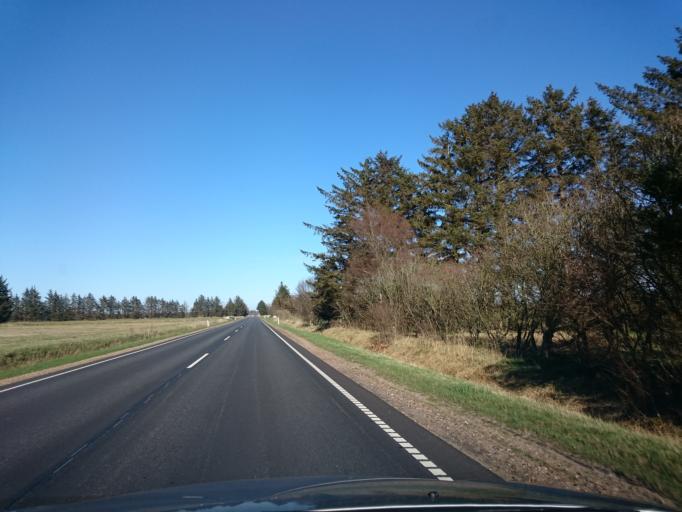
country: DK
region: North Denmark
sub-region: Hjorring Kommune
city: Sindal
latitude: 57.5927
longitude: 10.2964
